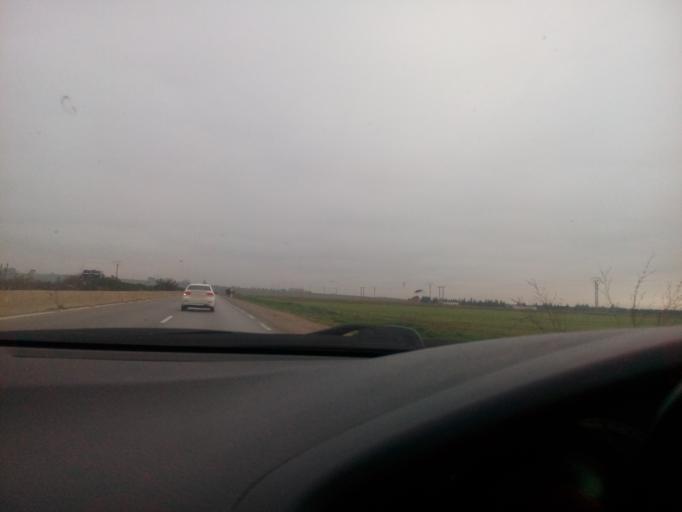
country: DZ
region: Oran
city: Bou Tlelis
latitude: 35.5517
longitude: -0.9518
